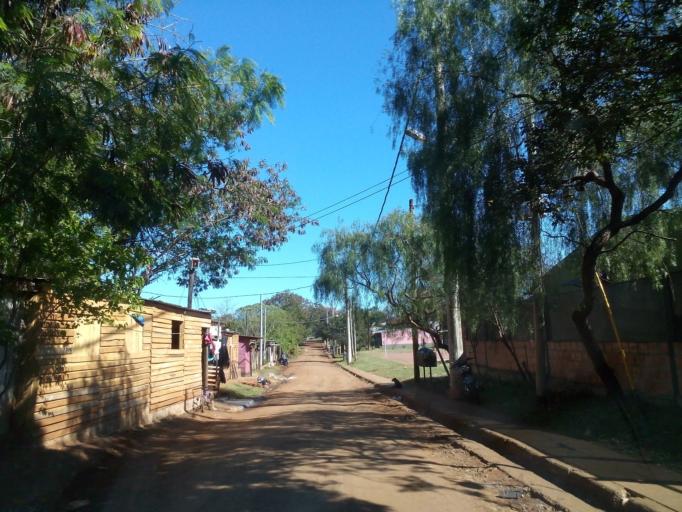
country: AR
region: Misiones
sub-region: Departamento de Capital
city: Posadas
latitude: -27.3864
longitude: -55.9420
